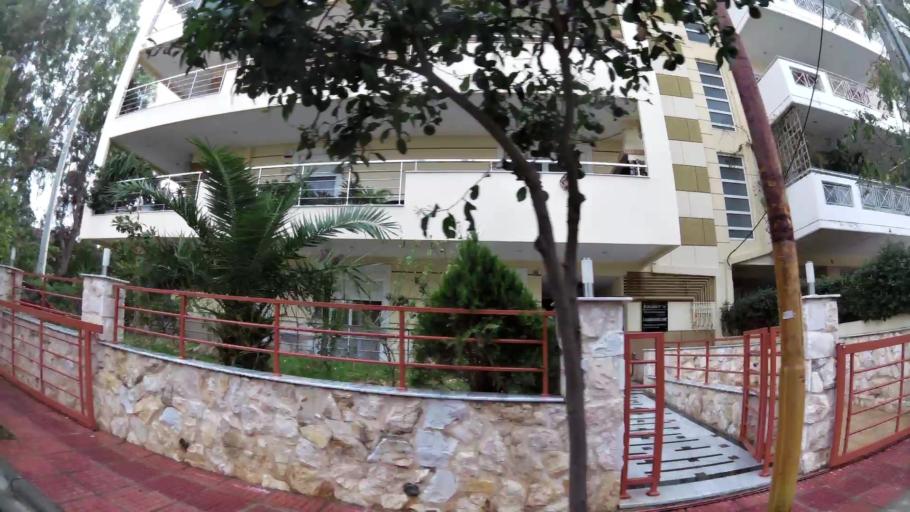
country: GR
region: Attica
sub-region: Nomarchia Athinas
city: Moskhaton
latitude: 37.9512
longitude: 23.6711
